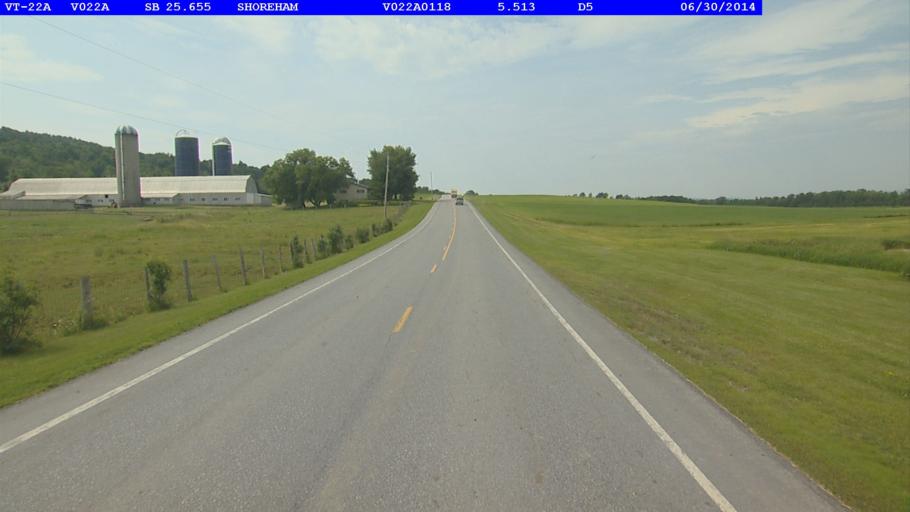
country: US
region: New York
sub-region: Essex County
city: Ticonderoga
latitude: 43.9285
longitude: -73.3102
